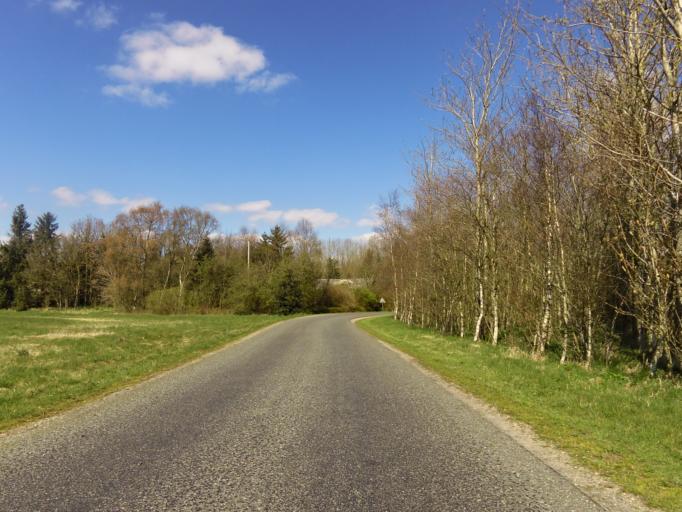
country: DK
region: South Denmark
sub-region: Esbjerg Kommune
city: Ribe
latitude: 55.3458
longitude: 8.8355
